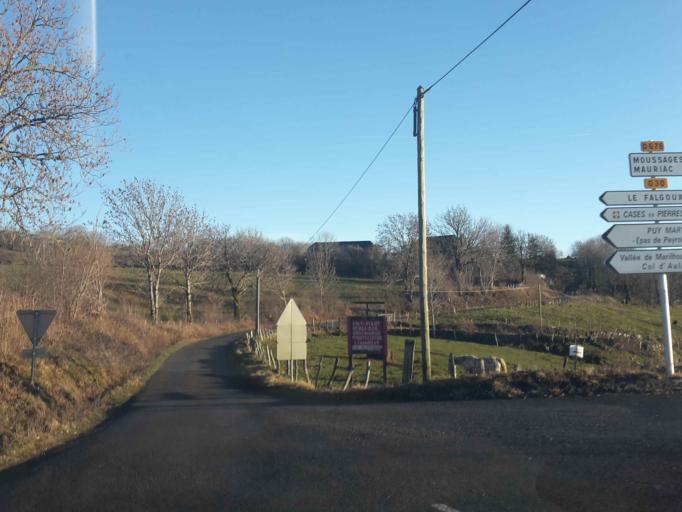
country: FR
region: Auvergne
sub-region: Departement du Cantal
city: Ydes
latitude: 45.2423
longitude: 2.5412
